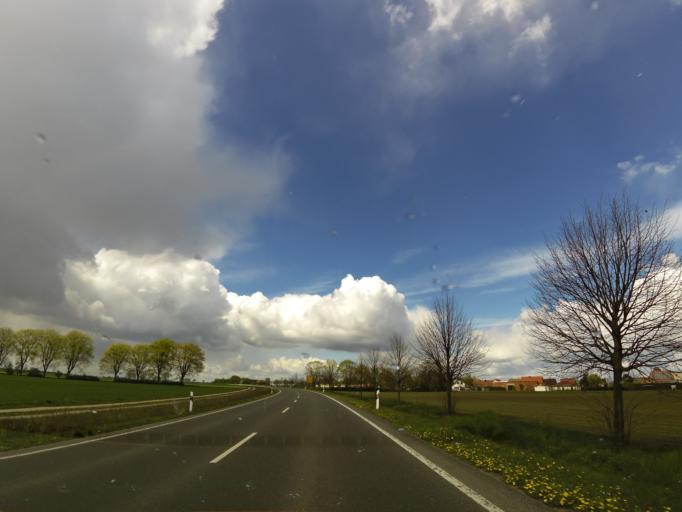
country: DE
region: Saxony-Anhalt
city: Hohendodeleben
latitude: 52.0735
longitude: 11.4805
